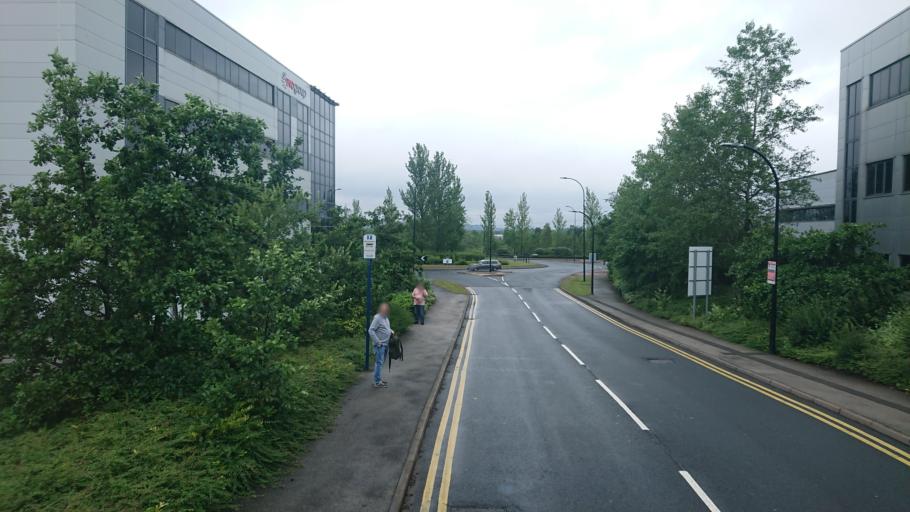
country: GB
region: England
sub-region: Rotherham
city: Orgreave
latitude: 53.3955
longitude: -1.3883
